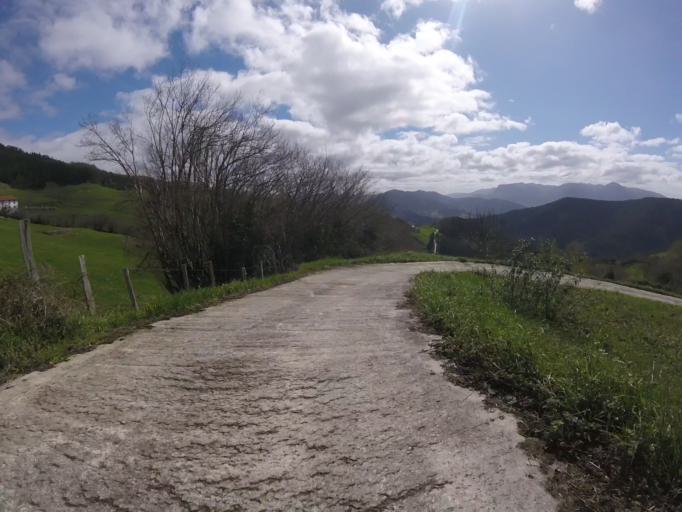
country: ES
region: Basque Country
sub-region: Provincia de Guipuzcoa
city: Albiztur
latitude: 43.1391
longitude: -2.1267
